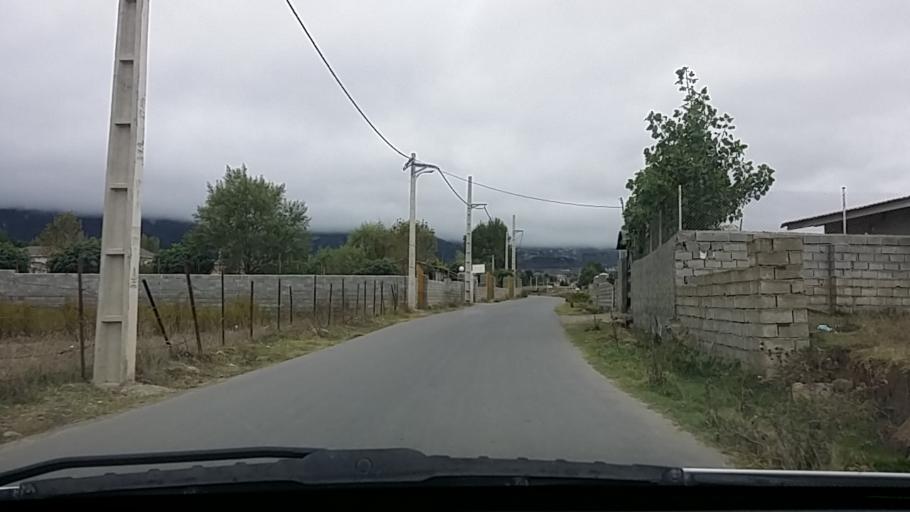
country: IR
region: Mazandaran
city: `Abbasabad
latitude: 36.5208
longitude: 51.1705
